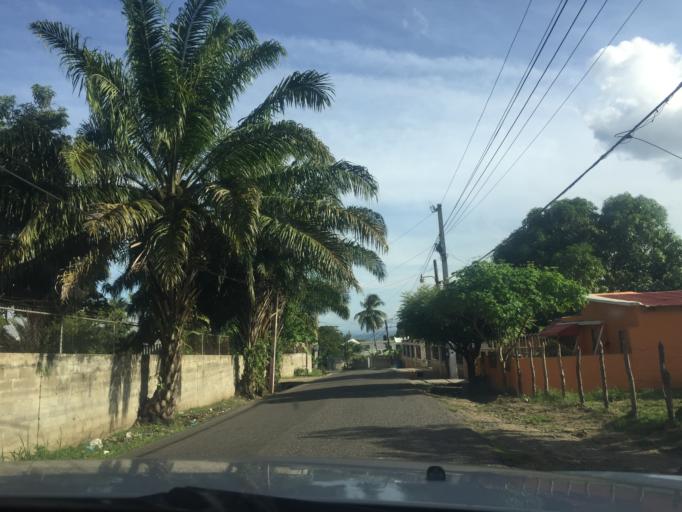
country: DO
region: Santiago
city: Tamboril
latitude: 19.4885
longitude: -70.6365
